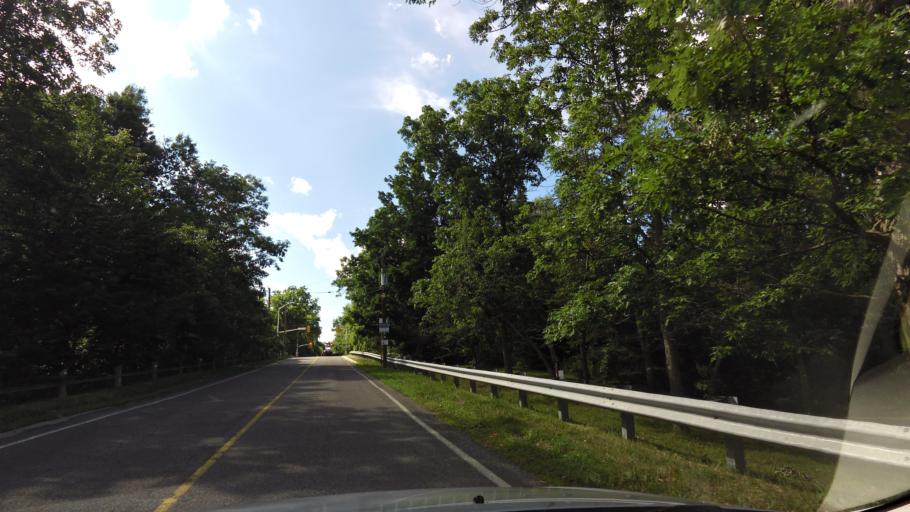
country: CA
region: Ontario
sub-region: Halton
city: Milton
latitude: 43.4566
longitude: -79.9147
